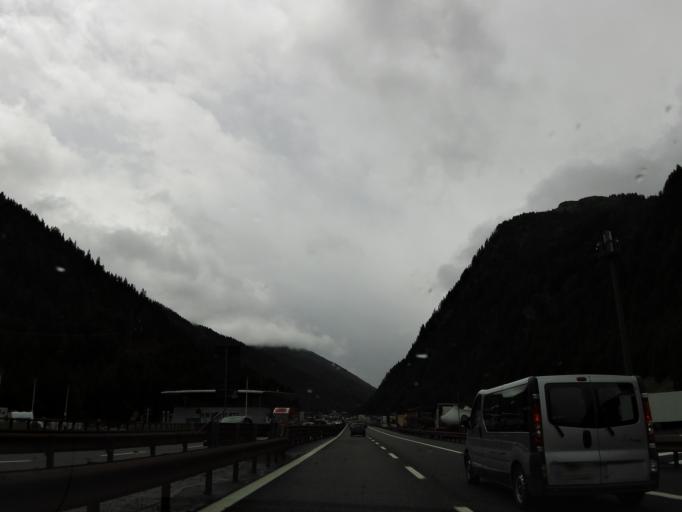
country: AT
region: Tyrol
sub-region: Politischer Bezirk Innsbruck Land
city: Gries am Brenner
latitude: 46.9965
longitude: 11.5020
